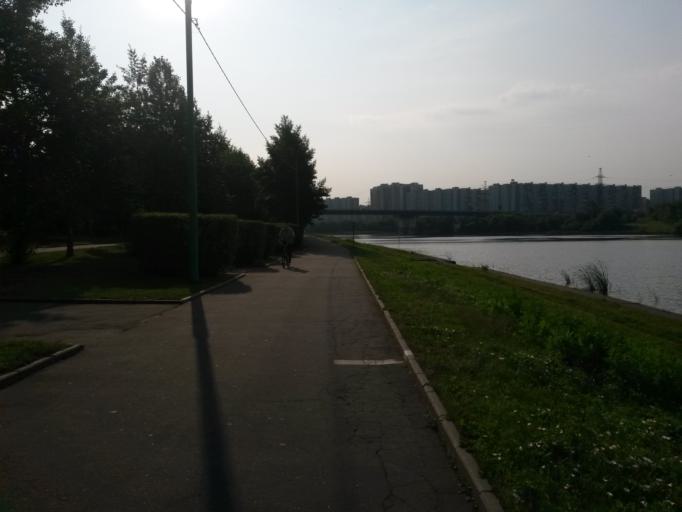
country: RU
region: Moscow
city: Brateyevo
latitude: 55.6413
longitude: 37.7401
